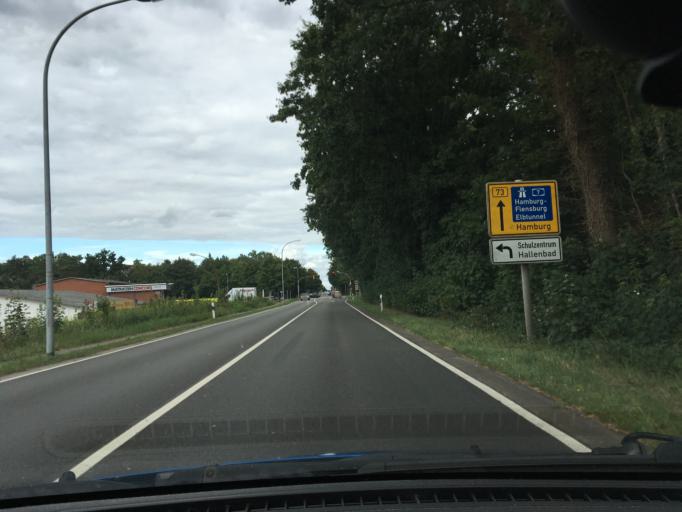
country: DE
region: Lower Saxony
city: Neu Wulmstorf
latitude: 53.4593
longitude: 9.7857
